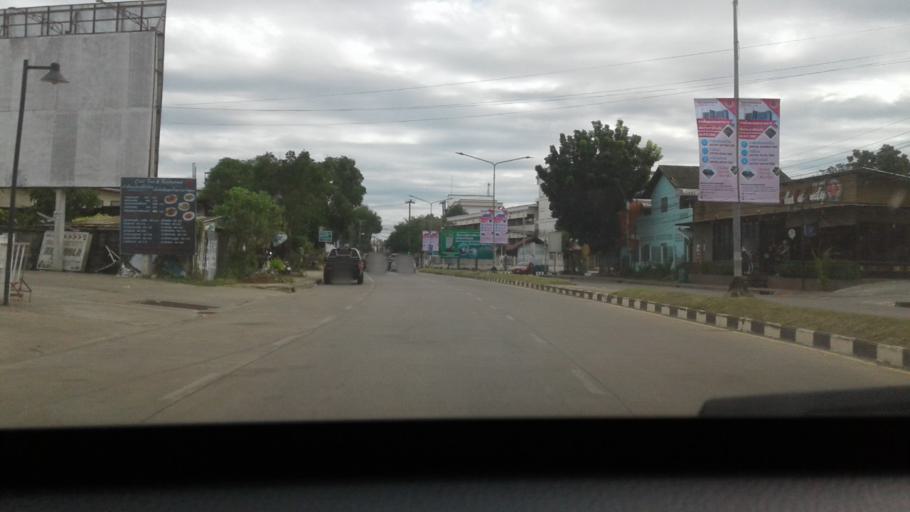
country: TH
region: Changwat Udon Thani
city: Udon Thani
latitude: 17.4193
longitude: 102.7855
